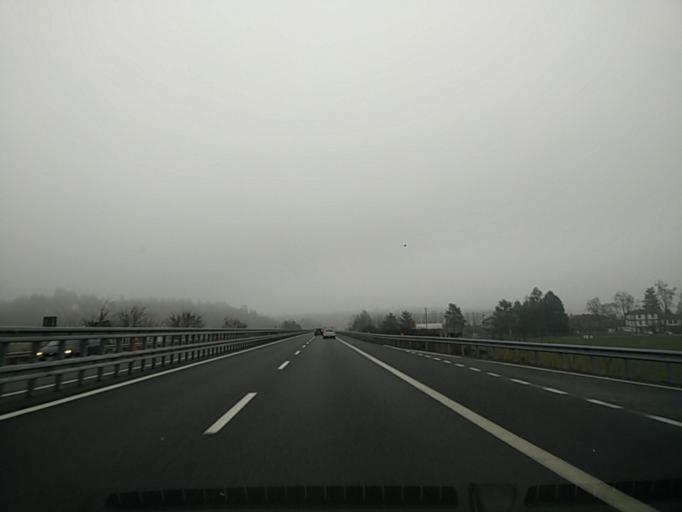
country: IT
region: Piedmont
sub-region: Provincia di Asti
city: Azzano d'Asti
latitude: 44.9084
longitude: 8.2696
